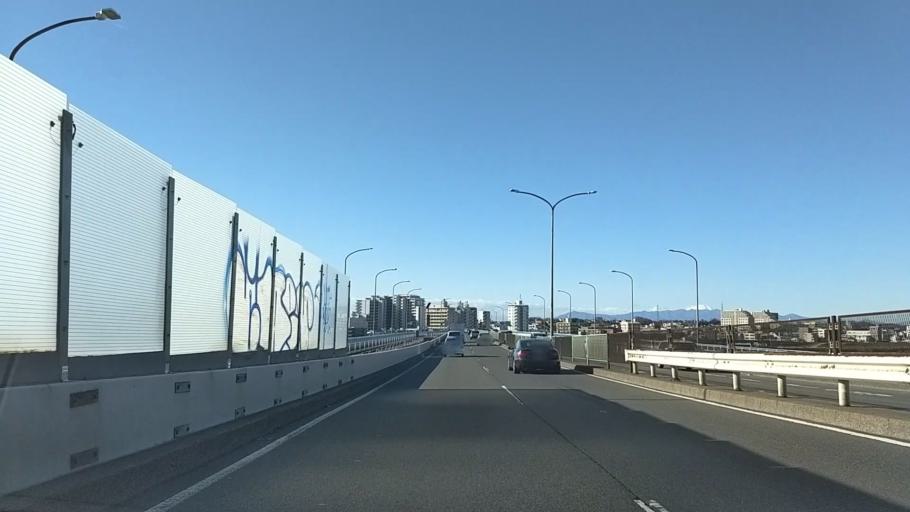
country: JP
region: Tokyo
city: Chofugaoka
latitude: 35.6130
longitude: 139.6243
